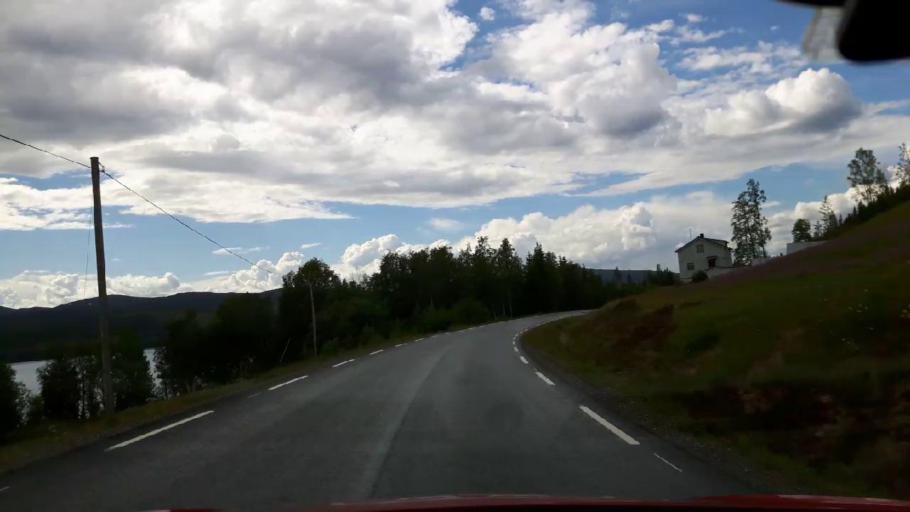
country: NO
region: Nord-Trondelag
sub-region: Lierne
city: Sandvika
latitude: 64.1015
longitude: 14.0073
